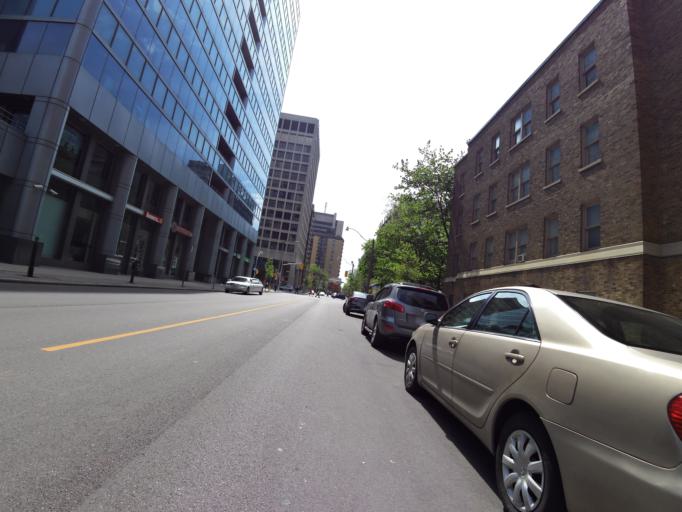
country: CA
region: Ontario
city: Toronto
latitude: 43.6567
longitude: -79.3879
